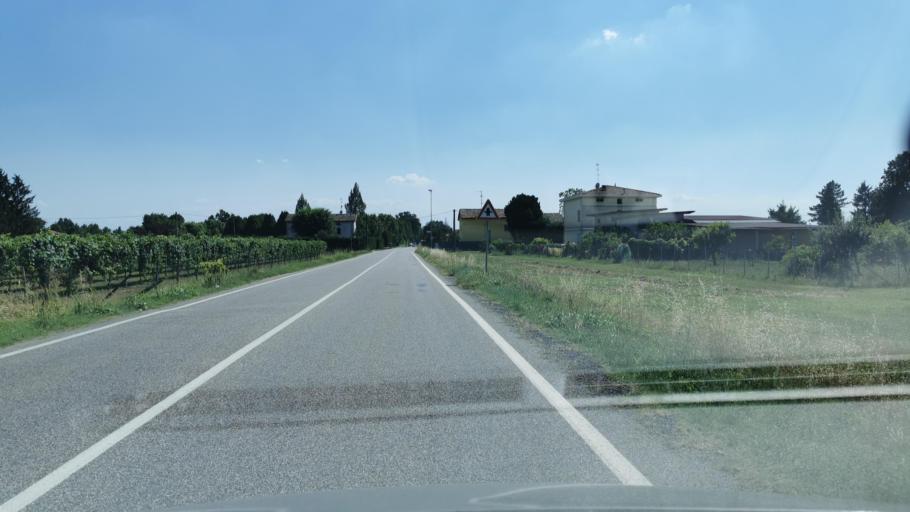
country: IT
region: Emilia-Romagna
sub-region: Provincia di Modena
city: Sam Marino
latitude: 44.7944
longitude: 10.9127
